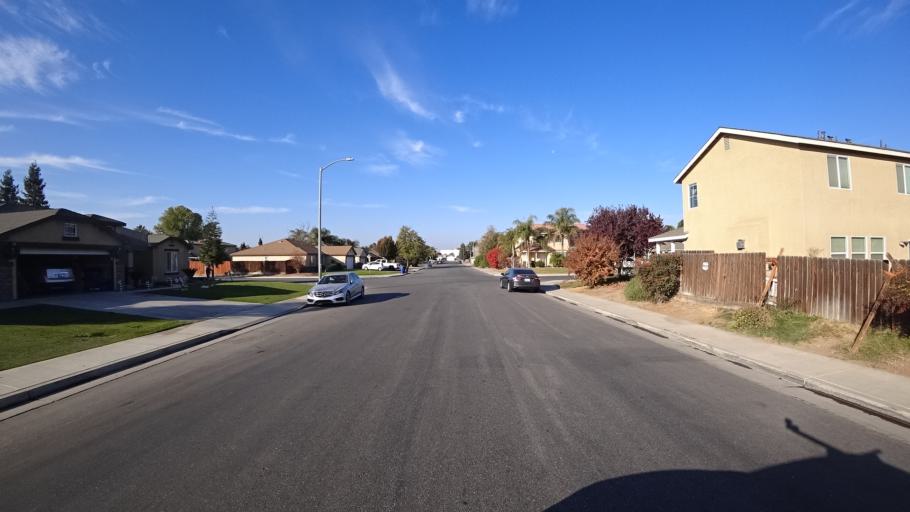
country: US
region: California
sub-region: Kern County
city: Greenfield
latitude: 35.2803
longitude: -119.0510
